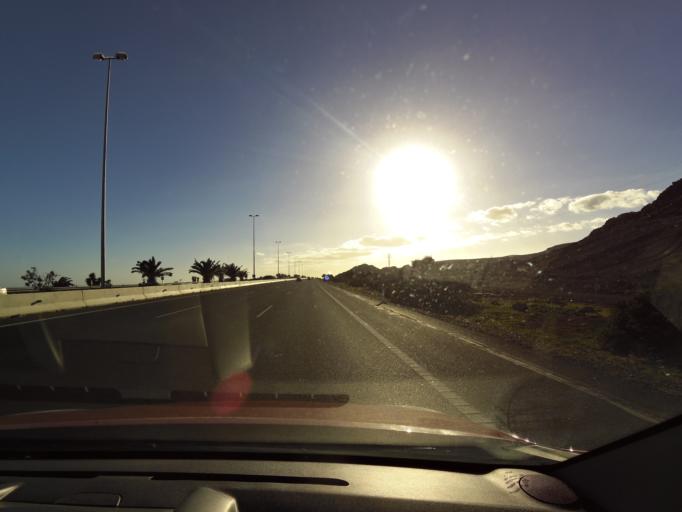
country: ES
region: Canary Islands
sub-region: Provincia de Las Palmas
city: Cruce de Arinaga
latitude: 27.8016
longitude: -15.4856
